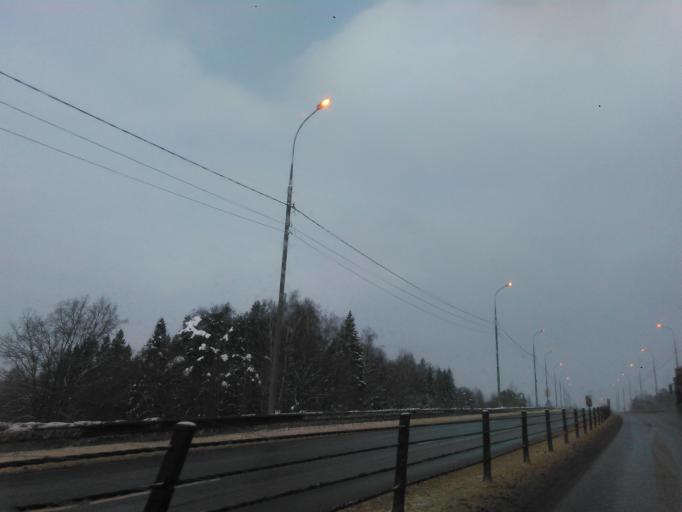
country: RU
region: Moskovskaya
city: Dedenevo
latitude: 56.2214
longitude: 37.5240
